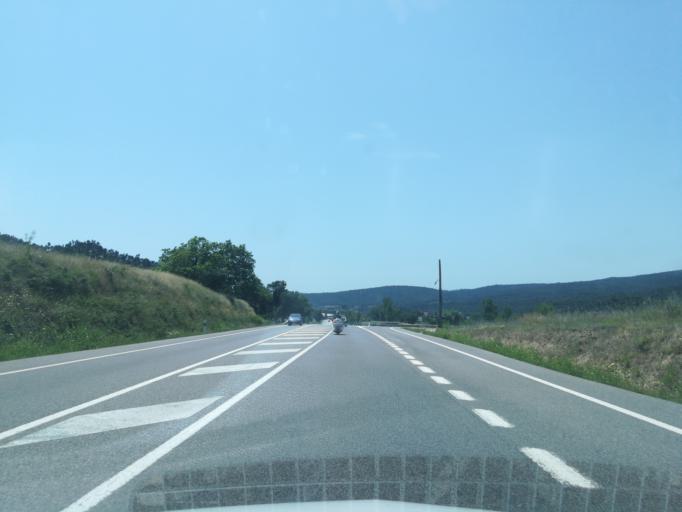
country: ES
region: Catalonia
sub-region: Provincia de Girona
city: la Jonquera
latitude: 42.4440
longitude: 2.8667
